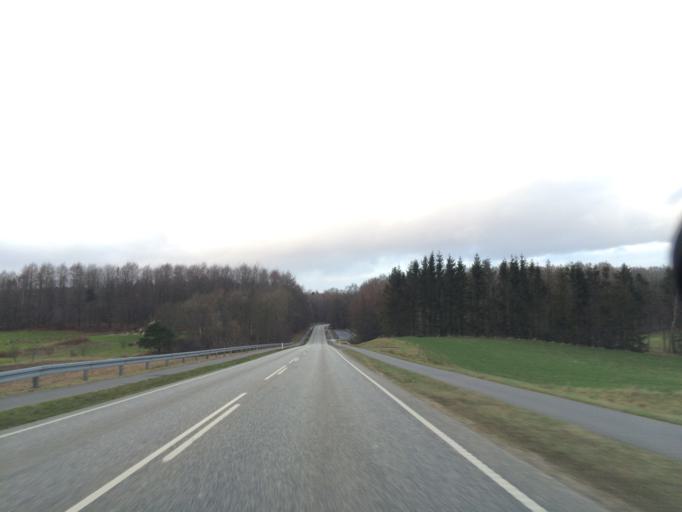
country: DK
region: Central Jutland
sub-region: Silkeborg Kommune
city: Virklund
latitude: 56.1118
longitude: 9.5697
